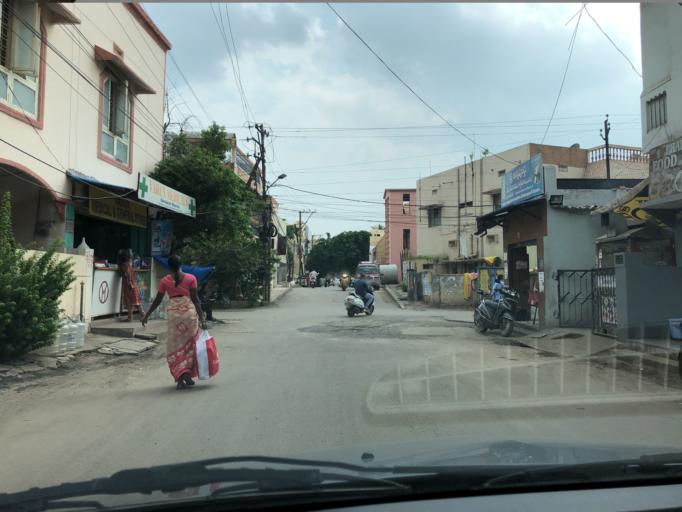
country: IN
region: Telangana
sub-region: Hyderabad
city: Malkajgiri
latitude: 17.4462
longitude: 78.4816
